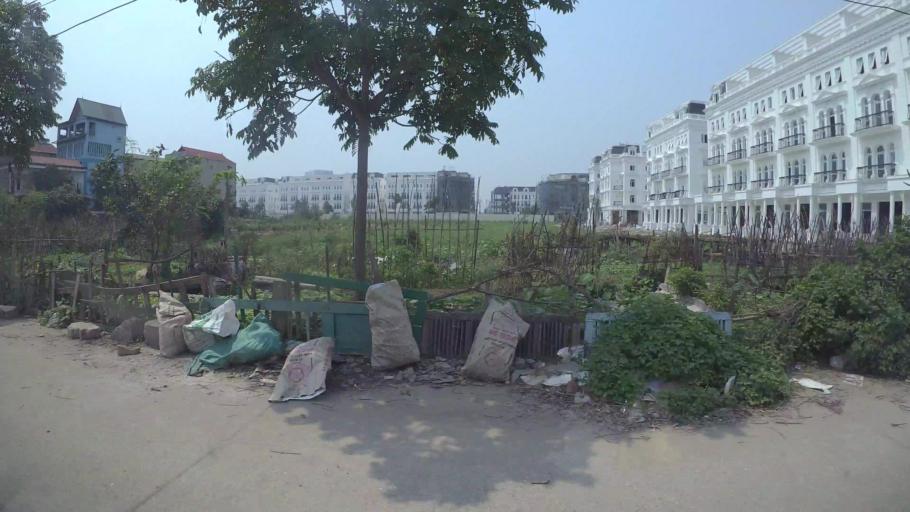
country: VN
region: Ha Noi
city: Ha Dong
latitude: 20.9866
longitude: 105.7647
